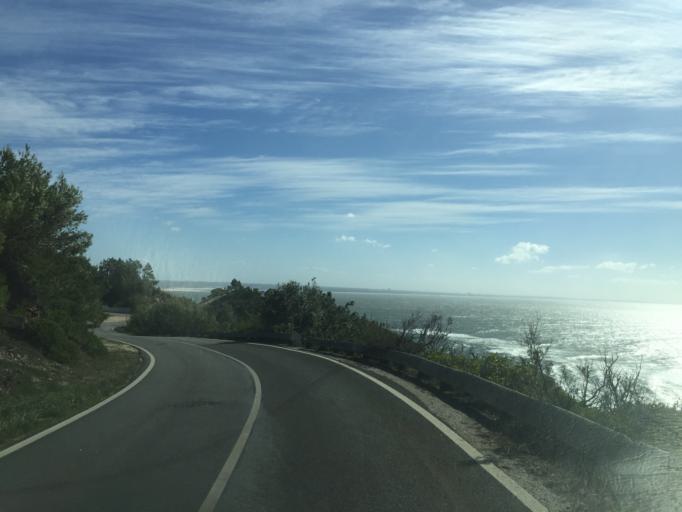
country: PT
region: Coimbra
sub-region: Figueira da Foz
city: Buarcos
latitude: 40.1808
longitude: -8.9056
